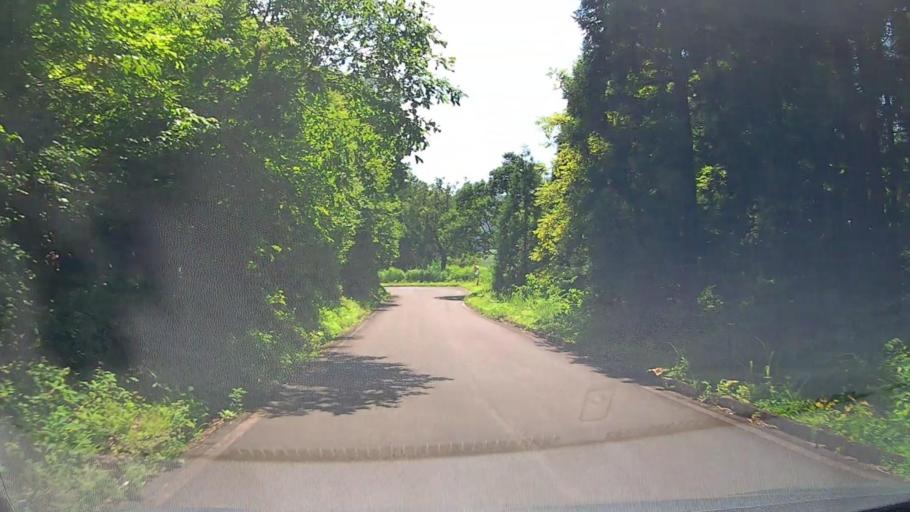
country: JP
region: Nagano
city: Iiyama
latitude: 36.9294
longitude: 138.4523
